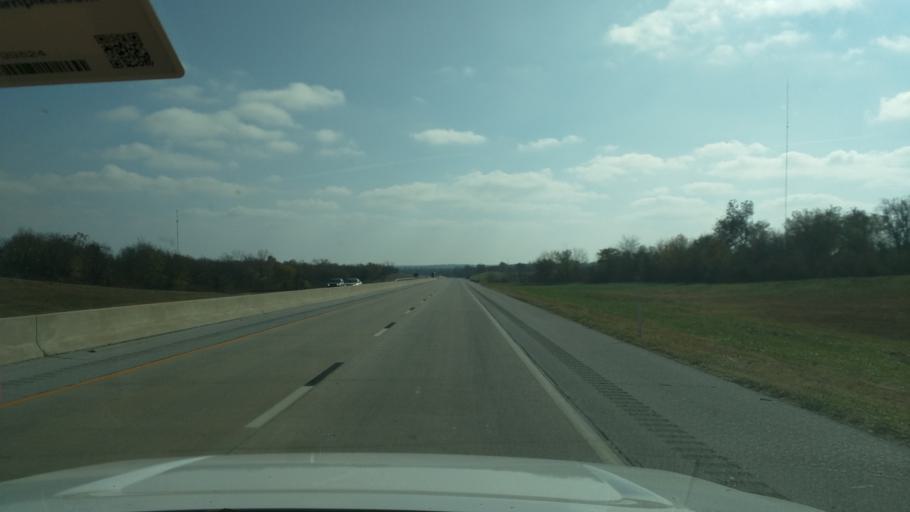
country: US
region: Oklahoma
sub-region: Wagoner County
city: Coweta
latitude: 35.9902
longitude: -95.6255
